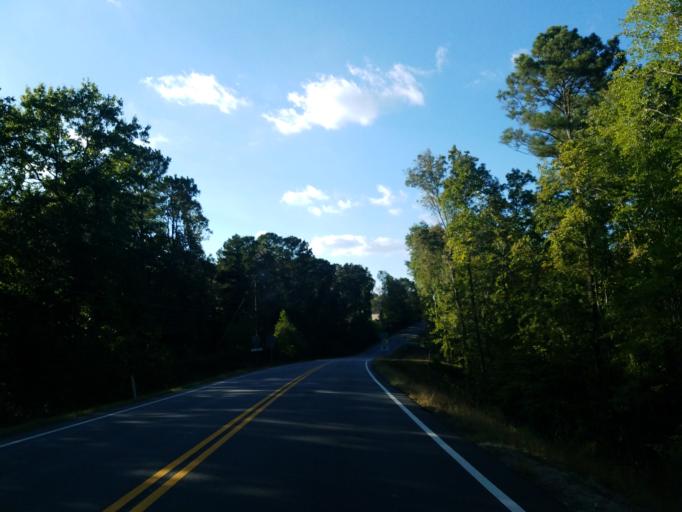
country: US
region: Georgia
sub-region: Bartow County
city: Cartersville
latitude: 34.0821
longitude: -84.8387
